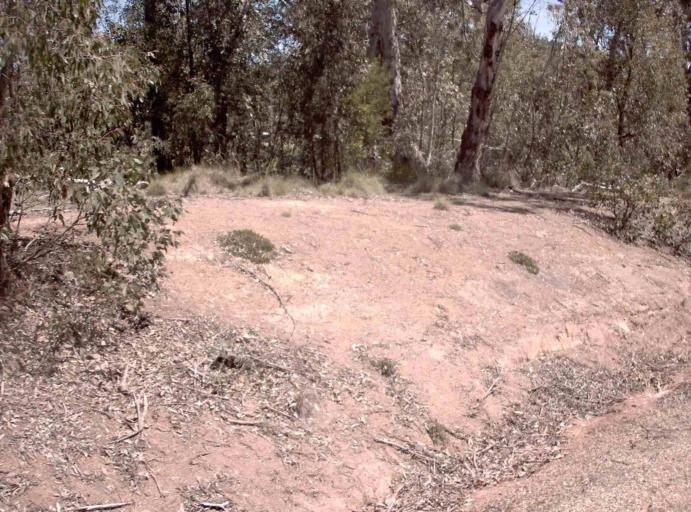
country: AU
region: New South Wales
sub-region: Snowy River
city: Jindabyne
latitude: -37.0761
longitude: 148.2602
